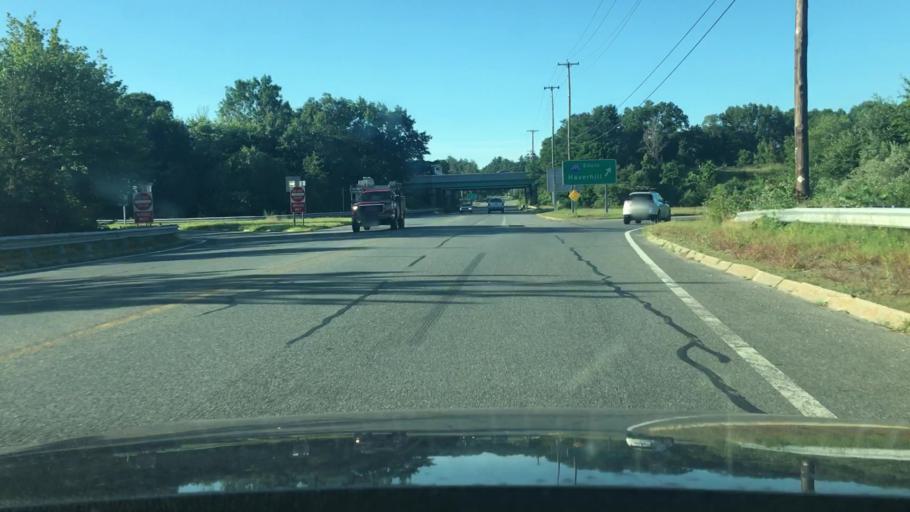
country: US
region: Massachusetts
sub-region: Essex County
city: Amesbury
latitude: 42.8413
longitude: -70.9371
